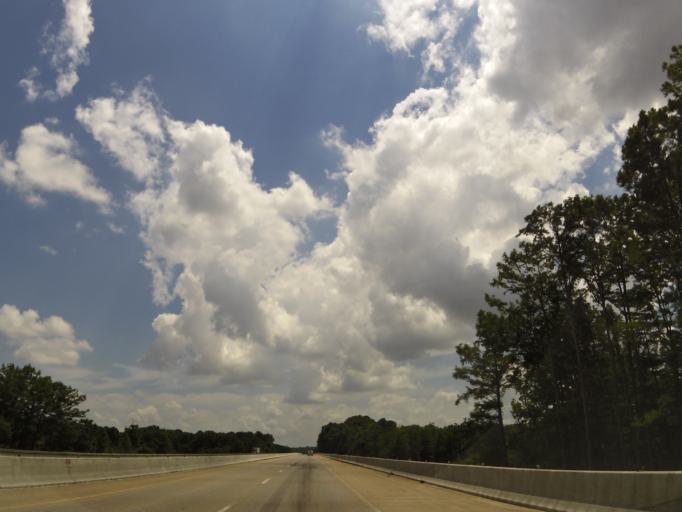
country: US
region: Tennessee
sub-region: Dyer County
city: Dyersburg
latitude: 35.9983
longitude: -89.3421
